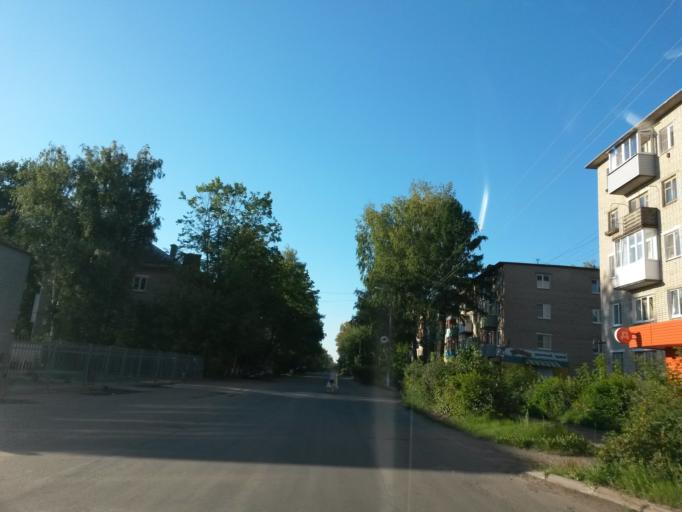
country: RU
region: Jaroslavl
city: Gavrilov-Yam
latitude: 57.3002
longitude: 39.8642
